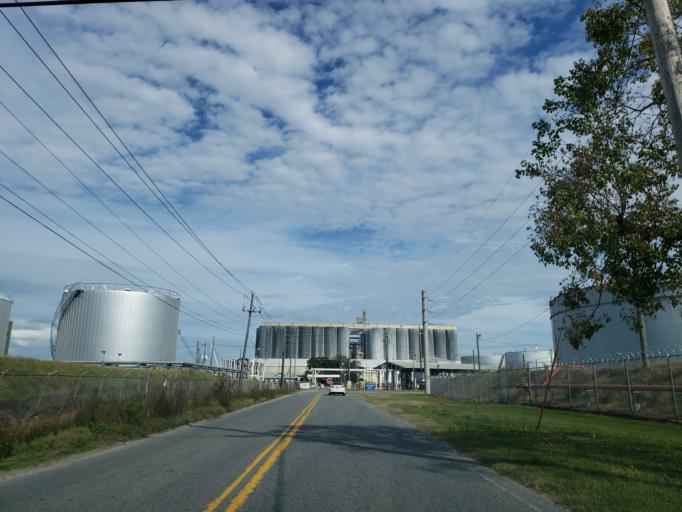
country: US
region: Georgia
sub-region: Chatham County
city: Savannah
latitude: 32.0984
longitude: -81.1205
